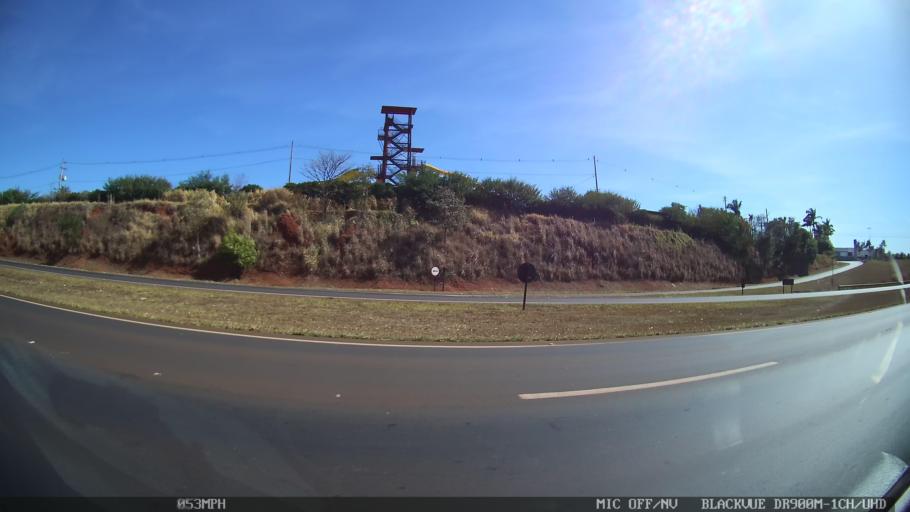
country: BR
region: Sao Paulo
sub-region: Barretos
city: Barretos
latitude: -20.5751
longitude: -48.5826
